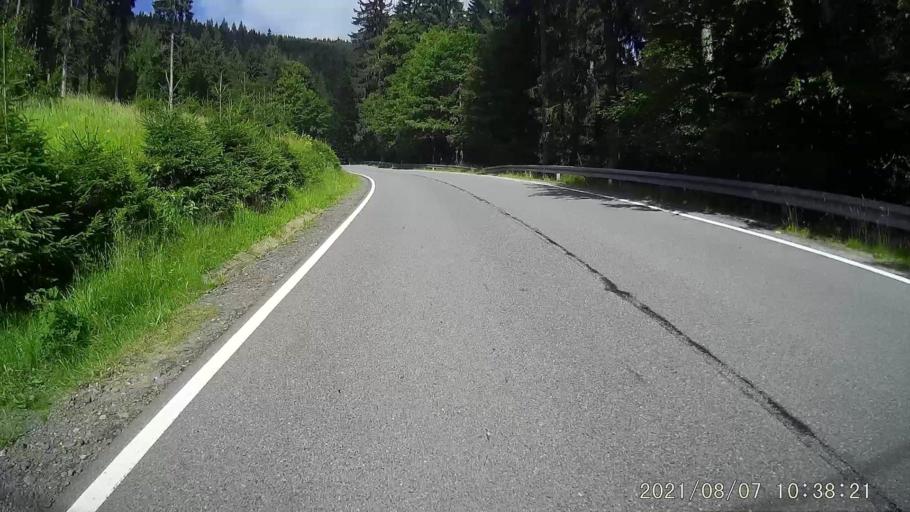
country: PL
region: Lower Silesian Voivodeship
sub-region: Powiat klodzki
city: Duszniki-Zdroj
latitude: 50.3509
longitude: 16.3709
